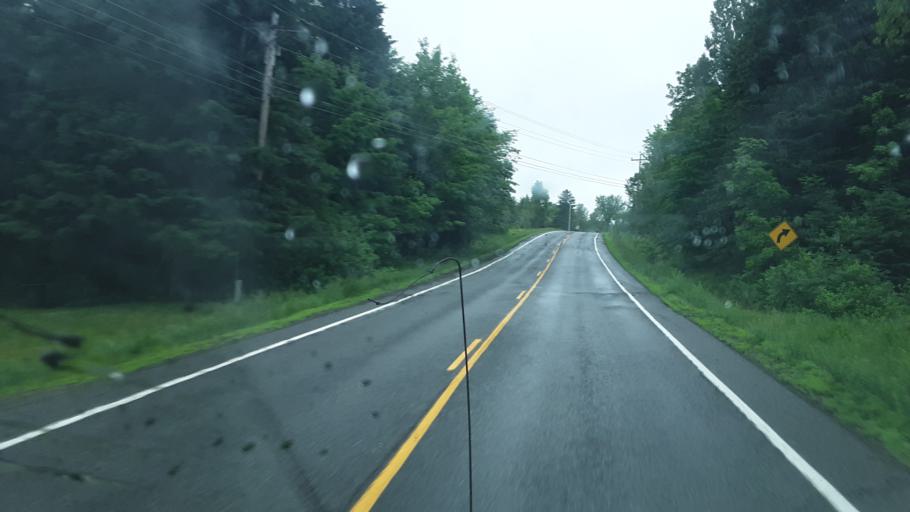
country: US
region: Maine
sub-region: Penobscot County
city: Patten
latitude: 46.0772
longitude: -68.4349
